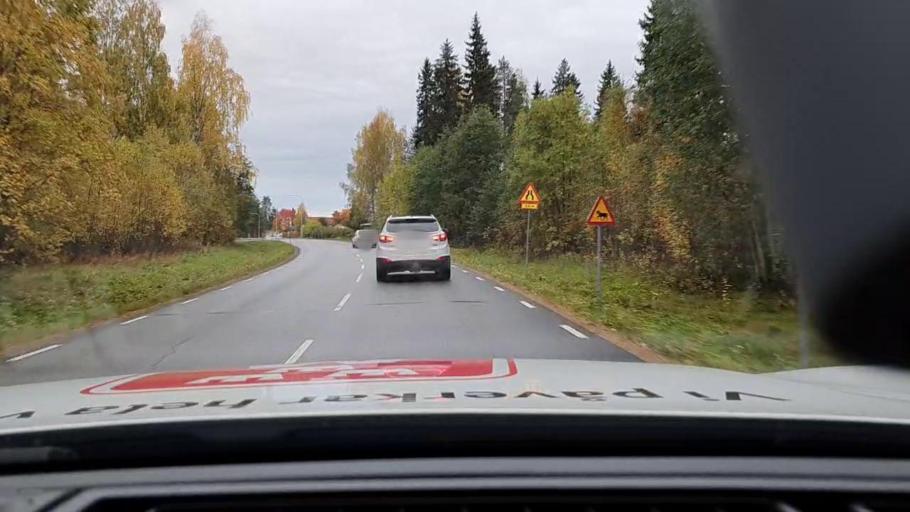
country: SE
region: Norrbotten
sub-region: Bodens Kommun
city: Saevast
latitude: 65.7787
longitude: 21.6922
